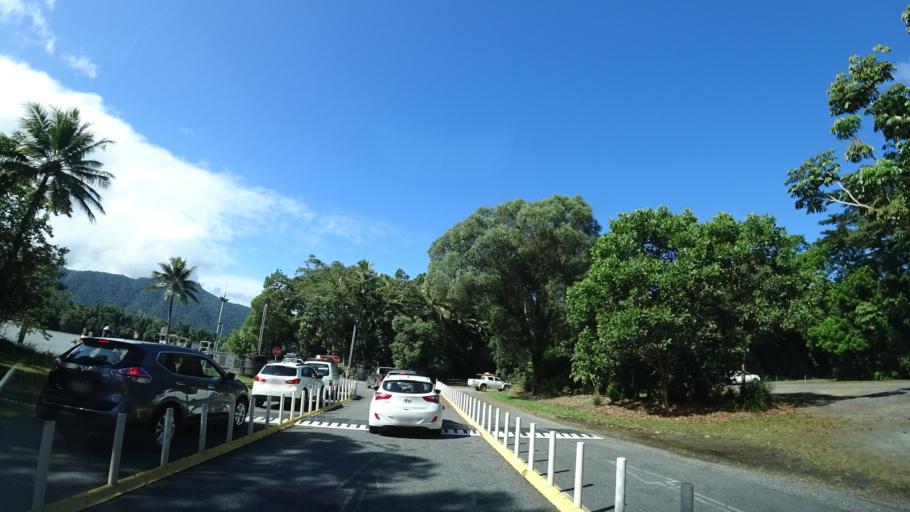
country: AU
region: Queensland
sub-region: Cairns
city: Port Douglas
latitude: -16.2612
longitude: 145.3971
